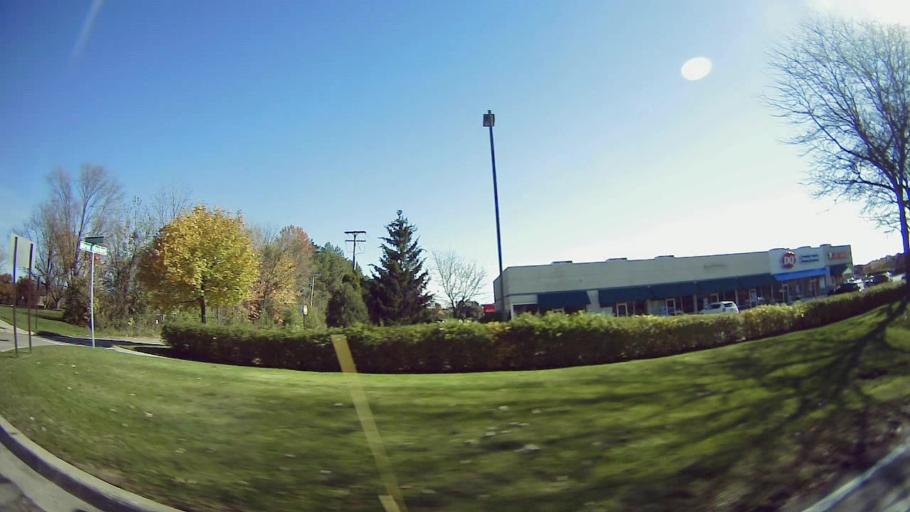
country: US
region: Michigan
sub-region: Oakland County
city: Farmington Hills
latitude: 42.5007
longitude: -83.3782
